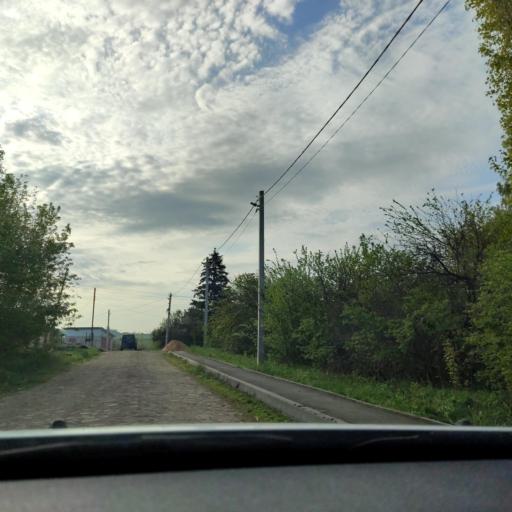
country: RU
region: Voronezj
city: Devitsa
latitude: 51.6411
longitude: 38.9561
